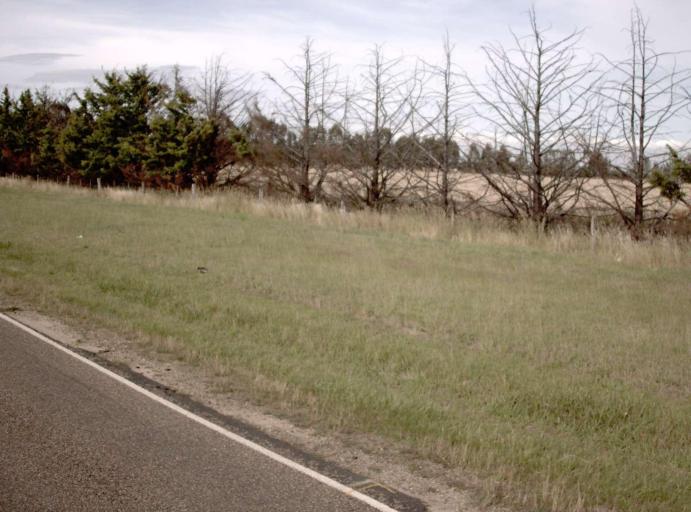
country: AU
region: Victoria
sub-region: Wellington
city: Heyfield
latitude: -38.0357
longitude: 146.6668
